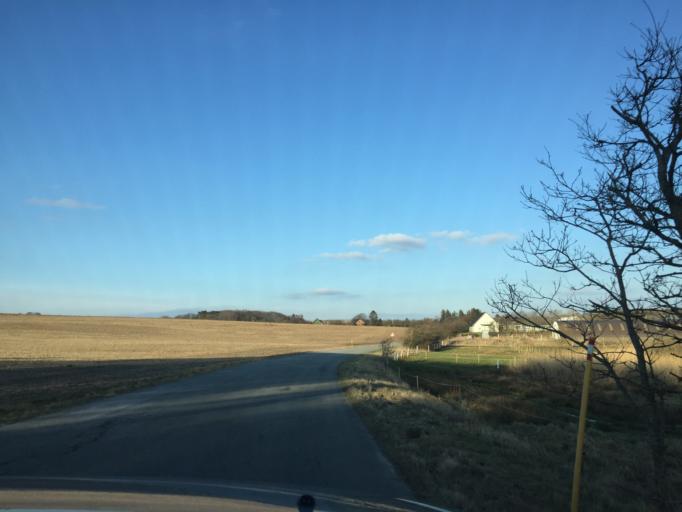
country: DK
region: Central Jutland
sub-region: Holstebro Kommune
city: Vinderup
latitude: 56.5796
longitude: 8.8052
